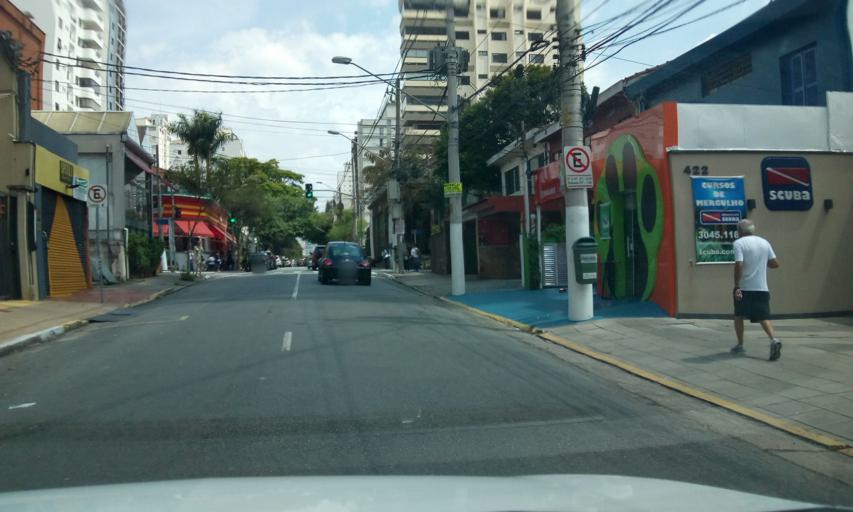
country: BR
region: Sao Paulo
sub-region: Sao Paulo
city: Sao Paulo
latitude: -23.5997
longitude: -46.6655
